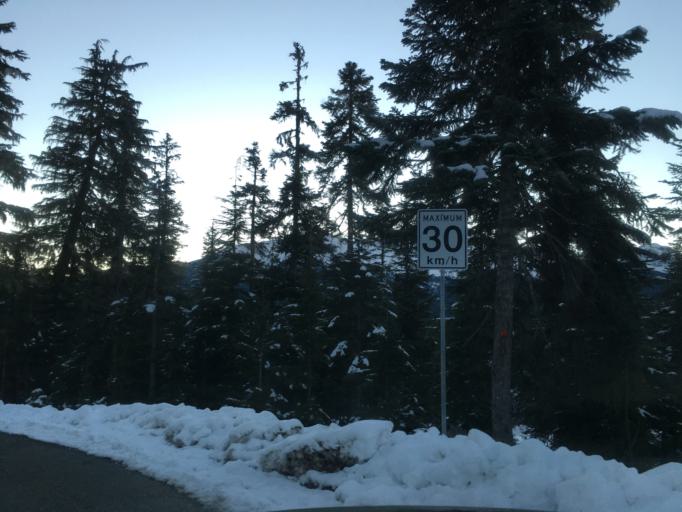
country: CA
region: British Columbia
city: Whistler
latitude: 50.1408
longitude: -123.1139
